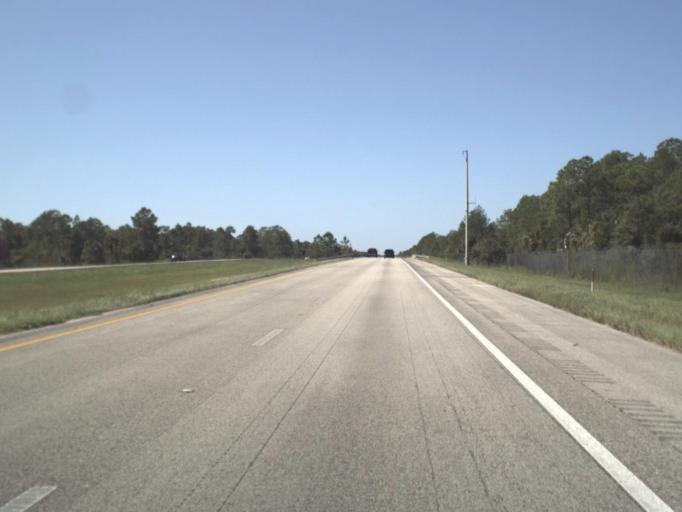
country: US
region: Florida
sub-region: Collier County
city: Orangetree
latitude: 26.1534
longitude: -81.4651
